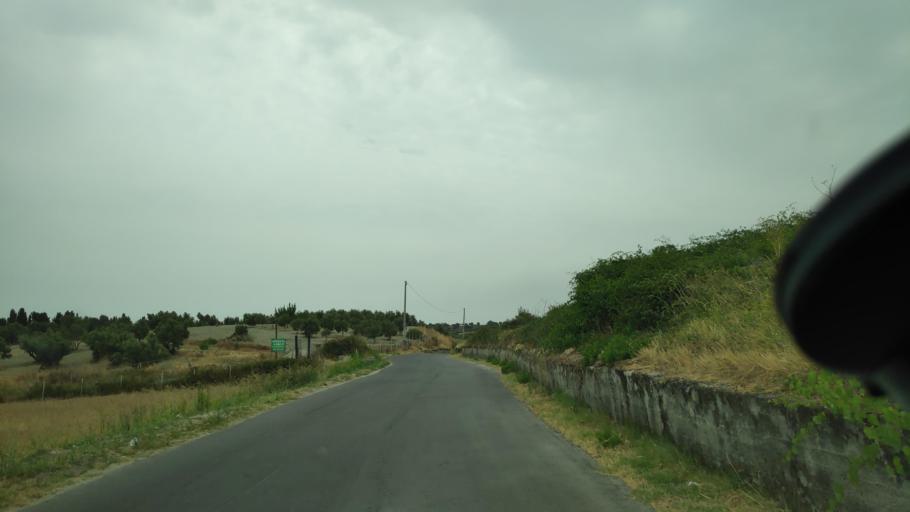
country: IT
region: Calabria
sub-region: Provincia di Catanzaro
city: Martelli-Laganosa
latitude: 38.6654
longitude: 16.5293
